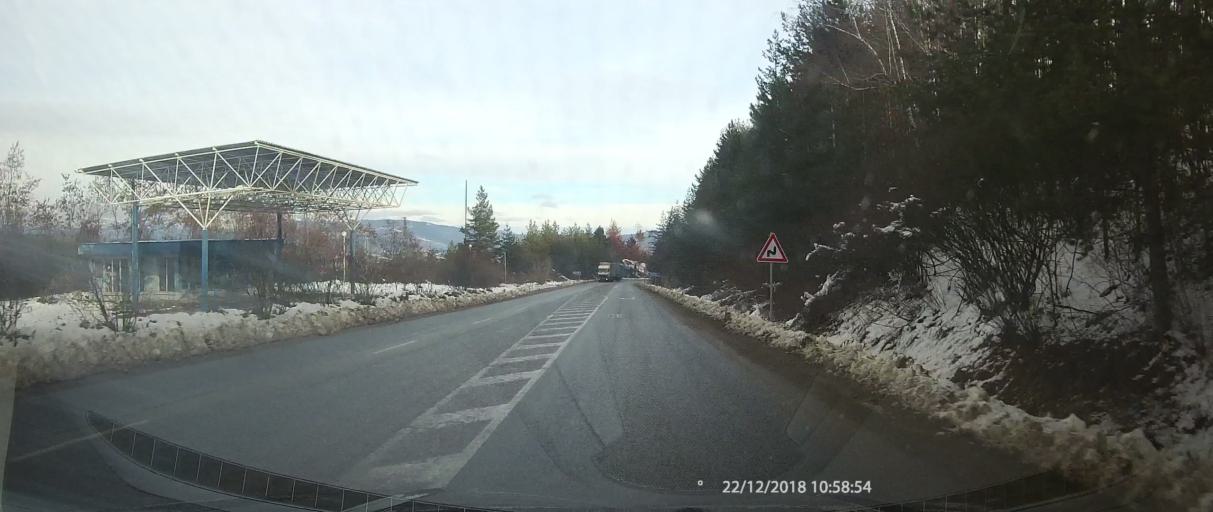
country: MK
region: Kriva Palanka
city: Kriva Palanka
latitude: 42.2218
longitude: 22.4740
